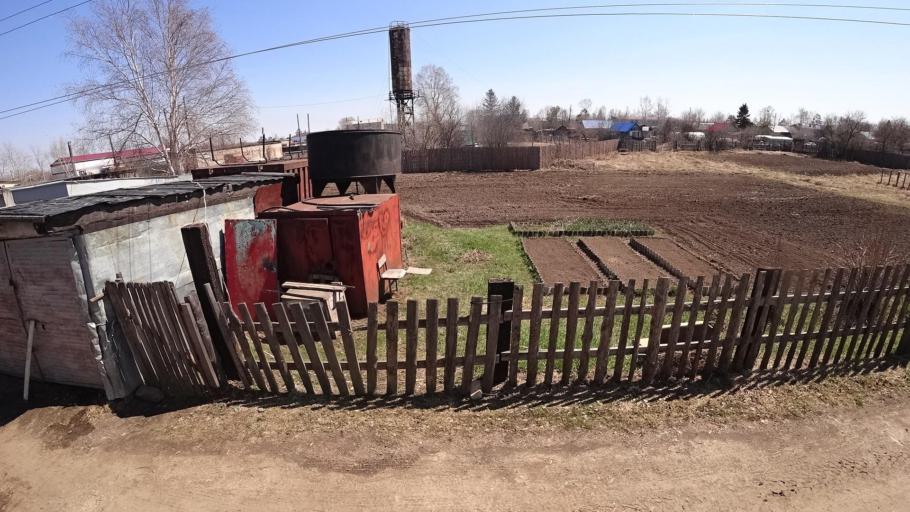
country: RU
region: Khabarovsk Krai
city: Khurba
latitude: 50.4079
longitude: 136.8871
